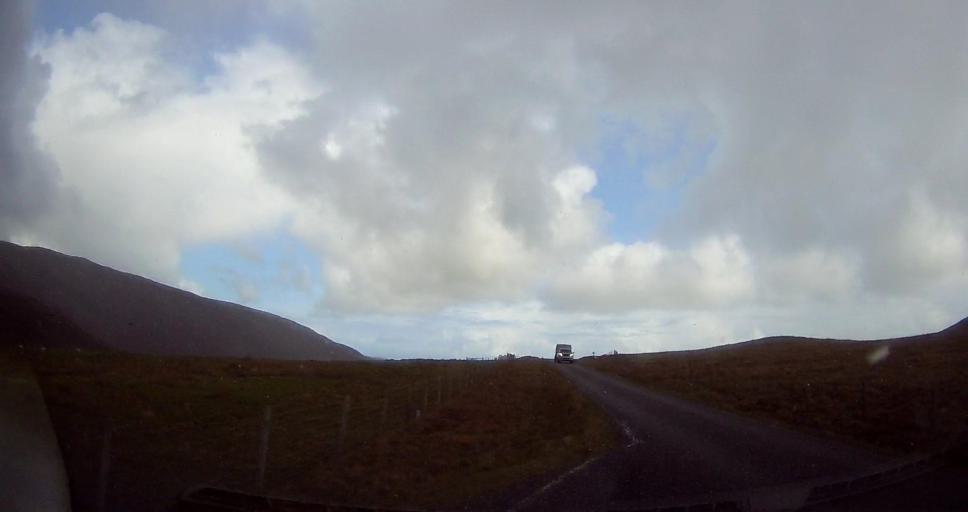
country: GB
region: Scotland
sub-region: Shetland Islands
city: Lerwick
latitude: 60.5563
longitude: -1.3397
